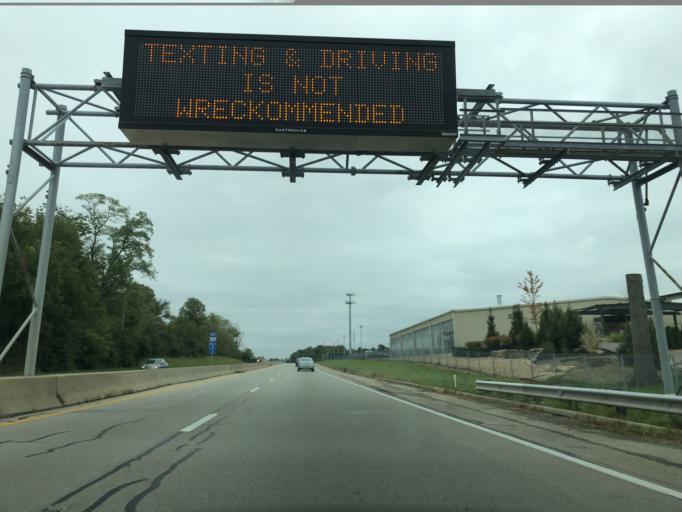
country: US
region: Ohio
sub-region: Hamilton County
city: Rossmoyne
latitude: 39.2252
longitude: -84.3883
